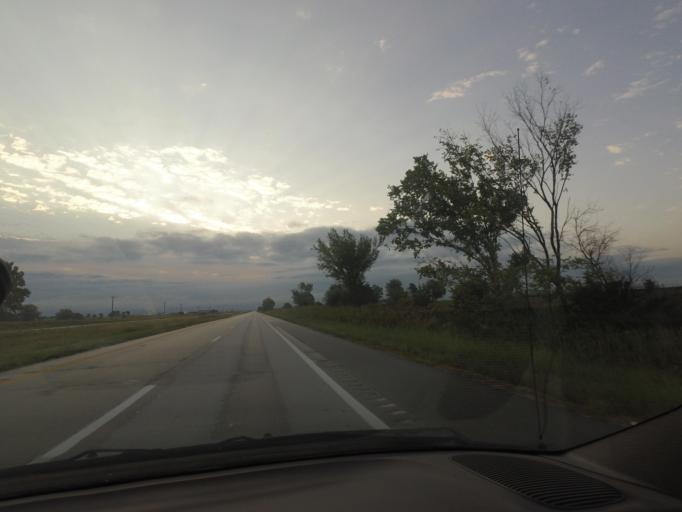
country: US
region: Missouri
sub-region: Shelby County
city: Shelbina
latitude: 39.7112
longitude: -92.1152
